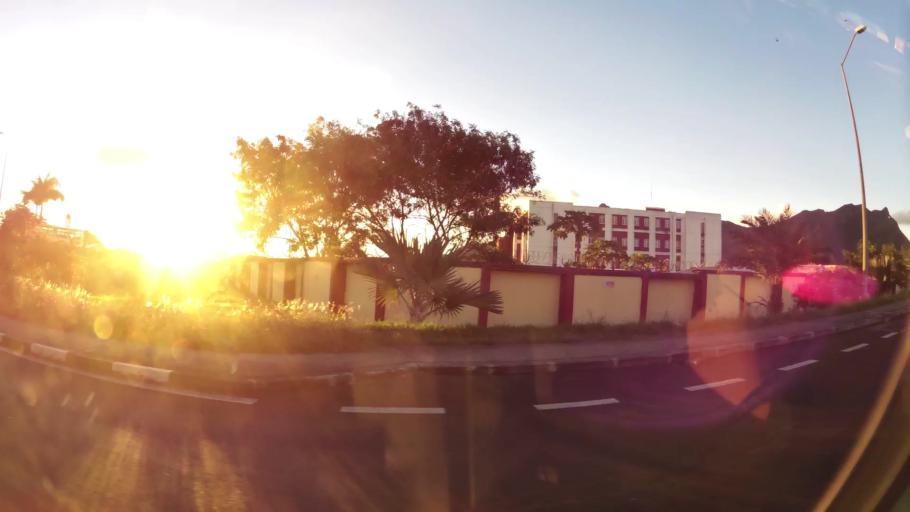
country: MU
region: Moka
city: Moka
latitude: -20.2311
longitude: 57.5021
